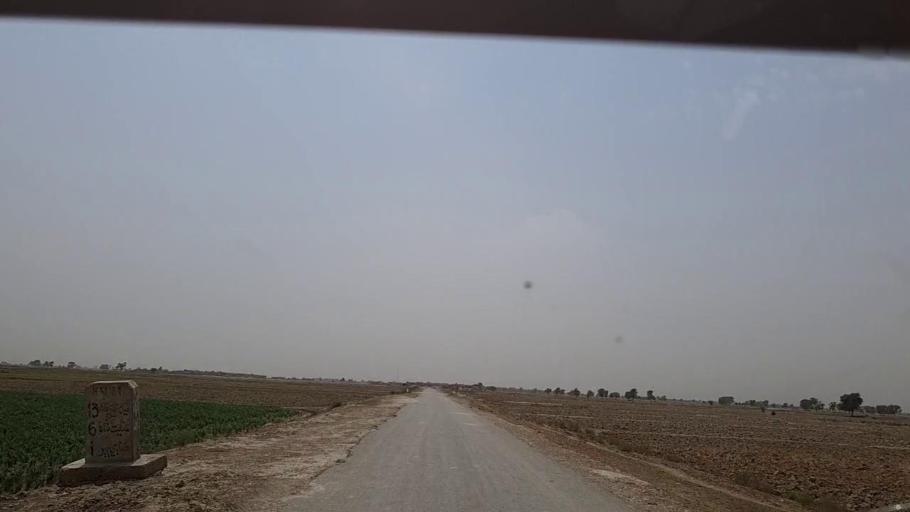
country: PK
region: Sindh
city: Khairpur Nathan Shah
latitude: 27.0177
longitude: 67.6141
